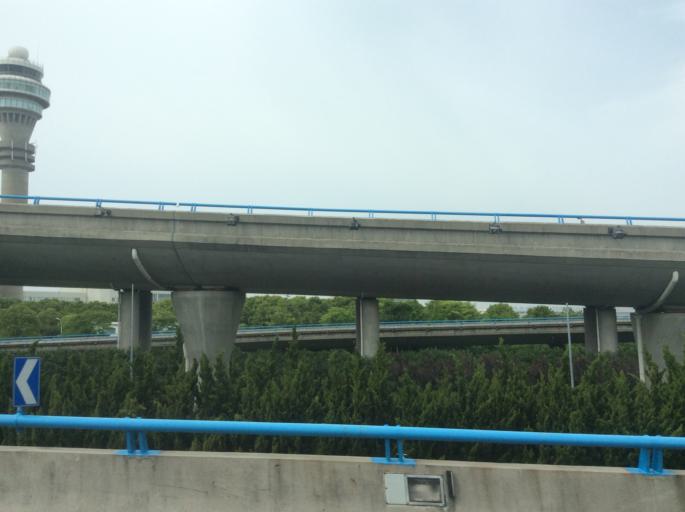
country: CN
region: Shanghai Shi
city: Laogang
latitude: 31.1459
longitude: 121.8028
